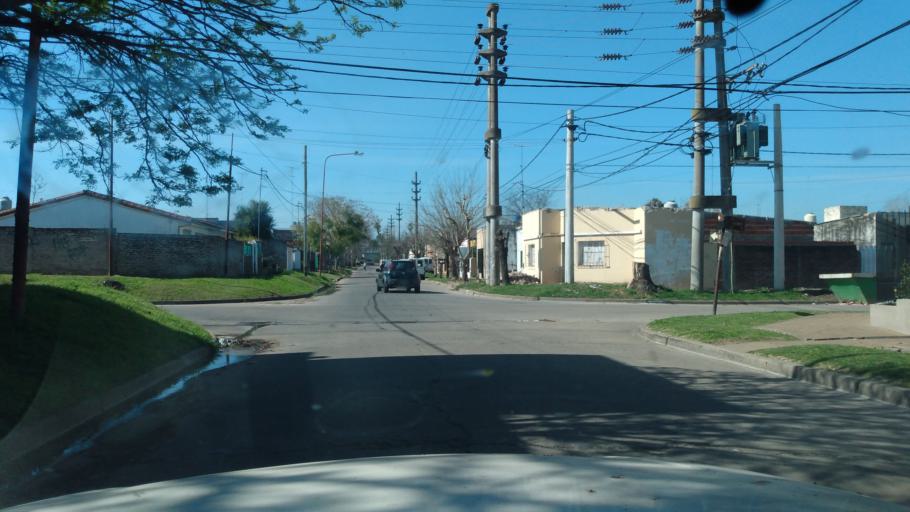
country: AR
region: Buenos Aires
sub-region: Partido de Lujan
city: Lujan
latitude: -34.5819
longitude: -59.1059
